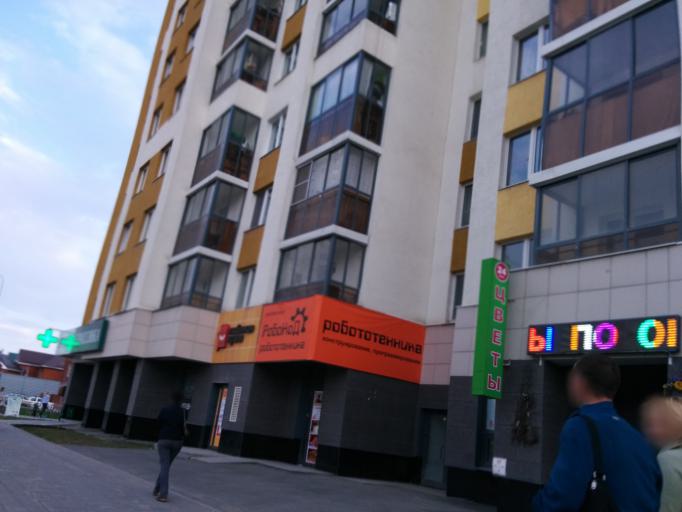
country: RU
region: Sverdlovsk
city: Sovkhoznyy
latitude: 56.7887
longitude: 60.5290
